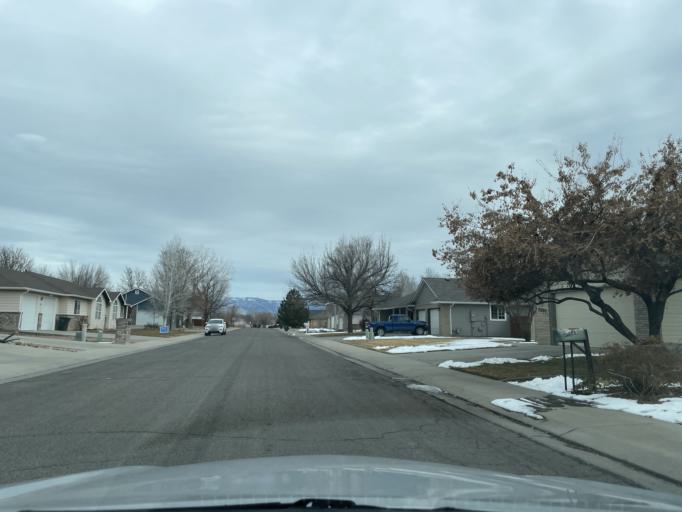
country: US
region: Colorado
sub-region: Mesa County
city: Grand Junction
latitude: 39.1017
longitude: -108.5828
